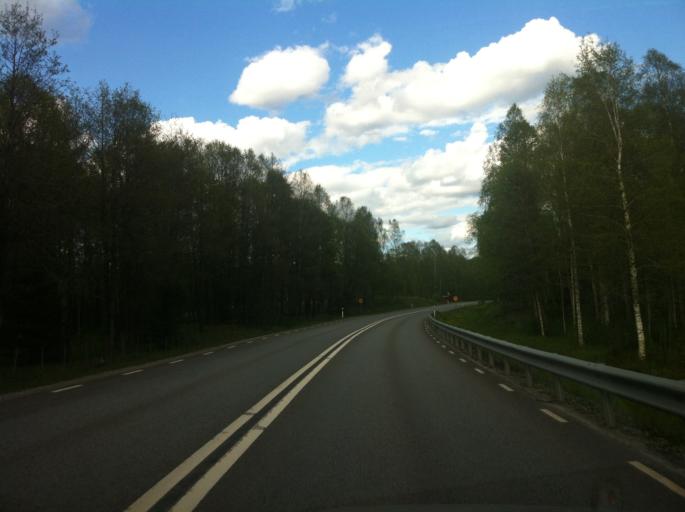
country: SE
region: Vaermland
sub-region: Filipstads Kommun
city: Filipstad
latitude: 59.7413
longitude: 14.2323
